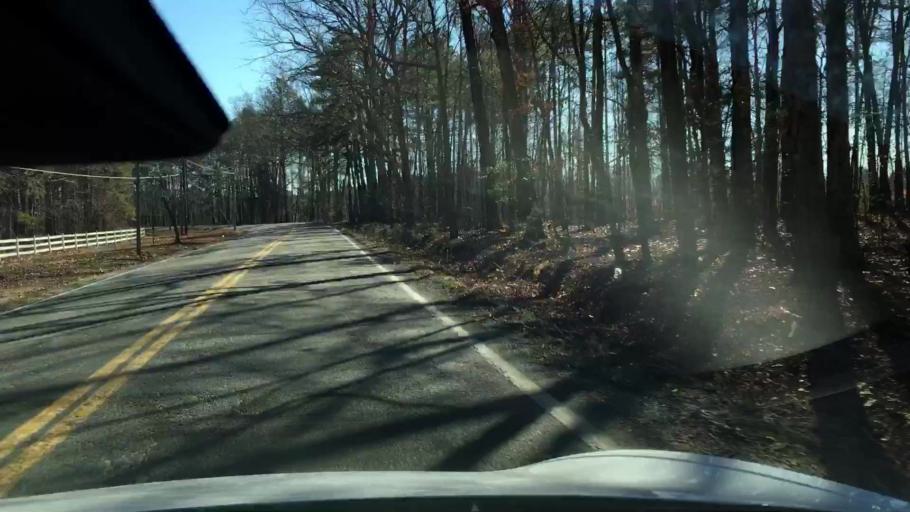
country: US
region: Virginia
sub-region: Henrico County
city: Short Pump
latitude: 37.5651
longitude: -77.7078
